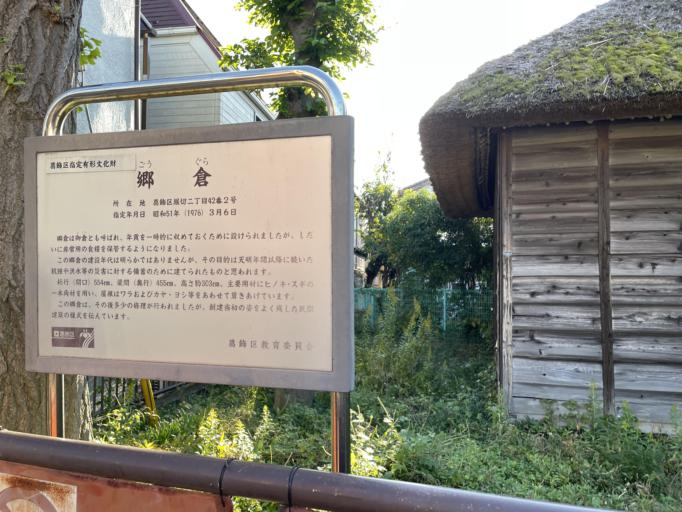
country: JP
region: Saitama
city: Yashio-shi
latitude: 35.7437
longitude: 139.8289
